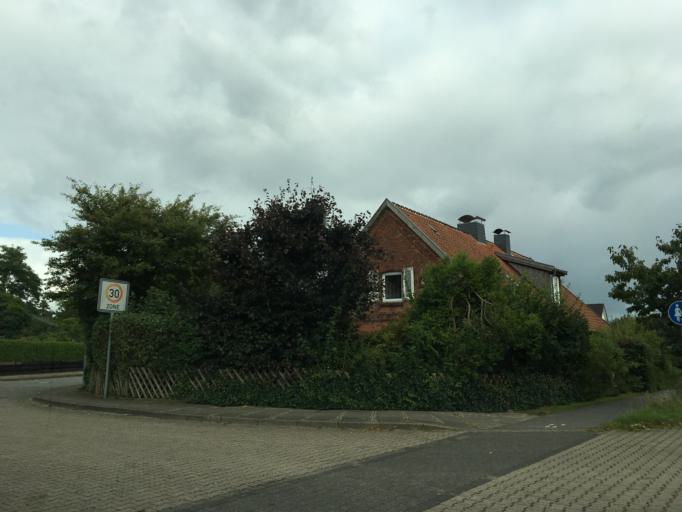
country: DE
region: Lower Saxony
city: Melbeck
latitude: 53.2106
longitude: 10.3918
